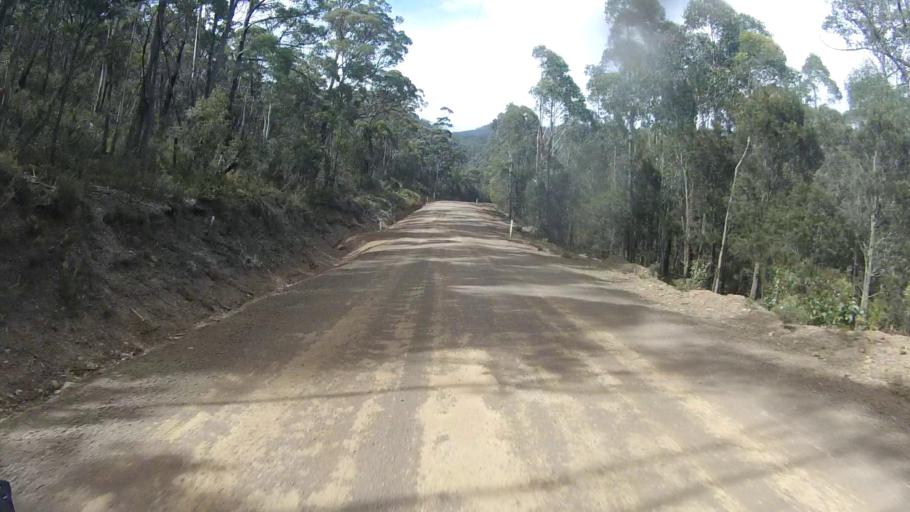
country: AU
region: Tasmania
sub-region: Sorell
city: Sorell
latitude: -42.6757
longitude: 147.8835
